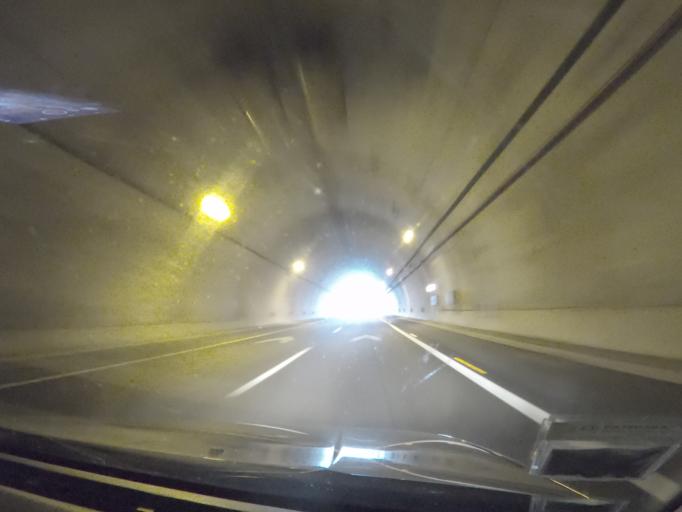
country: ES
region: Castille and Leon
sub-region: Provincia de Leon
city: Villafranca del Bierzo
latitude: 42.6084
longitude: -6.8208
